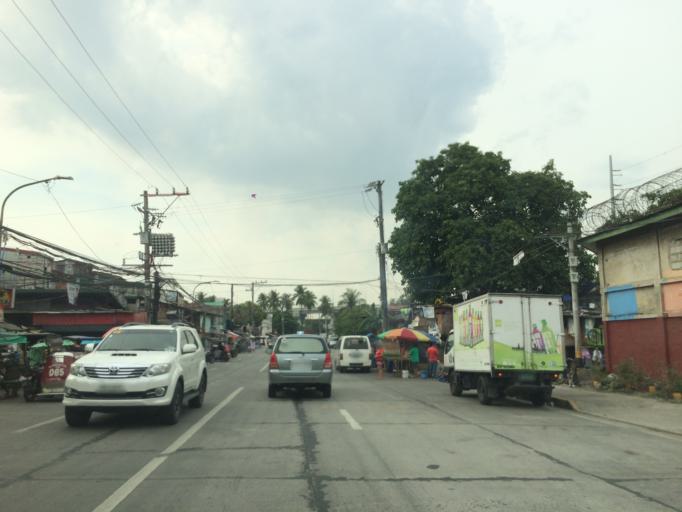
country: PH
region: Calabarzon
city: Del Monte
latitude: 14.6418
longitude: 121.0050
